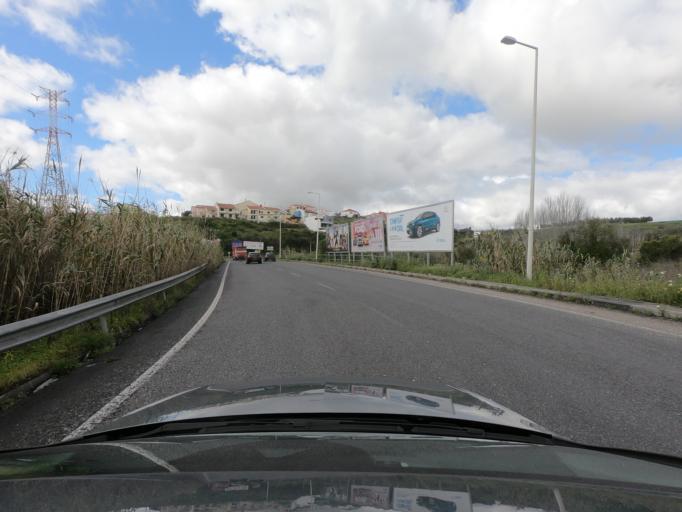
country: PT
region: Lisbon
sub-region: Loures
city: Santa Iria da Azoia
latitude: 38.8497
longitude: -9.0901
